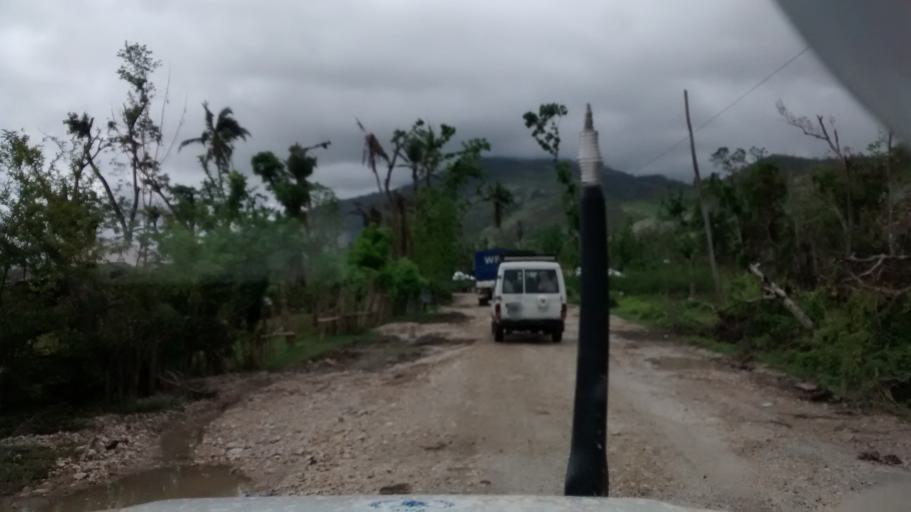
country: HT
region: Grandans
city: Moron
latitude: 18.5986
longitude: -74.1937
